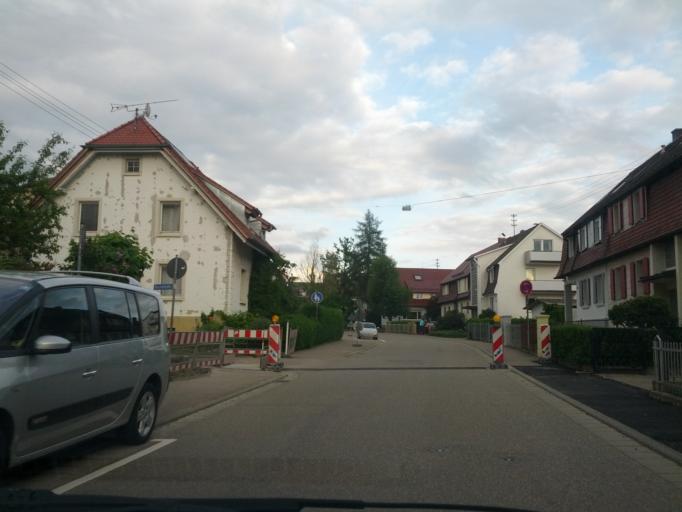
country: DE
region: Baden-Wuerttemberg
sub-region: Freiburg Region
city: Denzlingen
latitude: 48.0686
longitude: 7.8906
